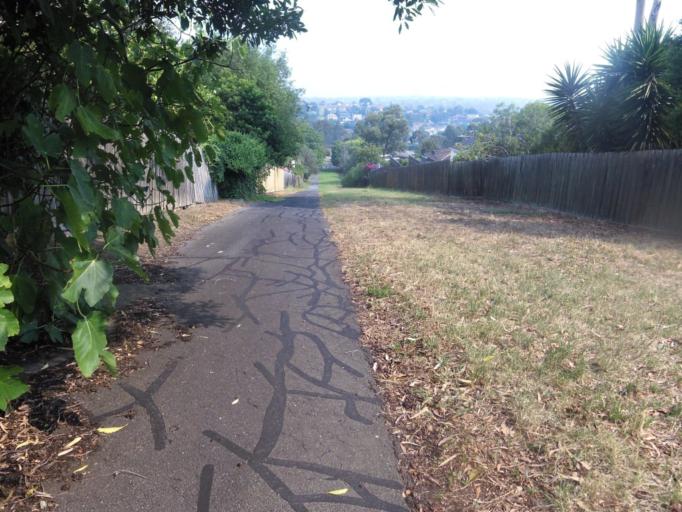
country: AU
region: Victoria
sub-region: Manningham
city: Bulleen
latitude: -37.7685
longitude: 145.0885
